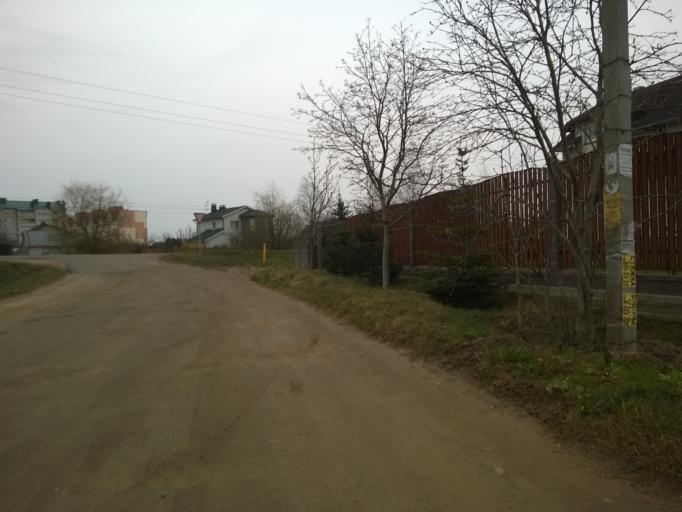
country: BY
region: Minsk
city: Slabada
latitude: 54.0064
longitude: 27.8670
